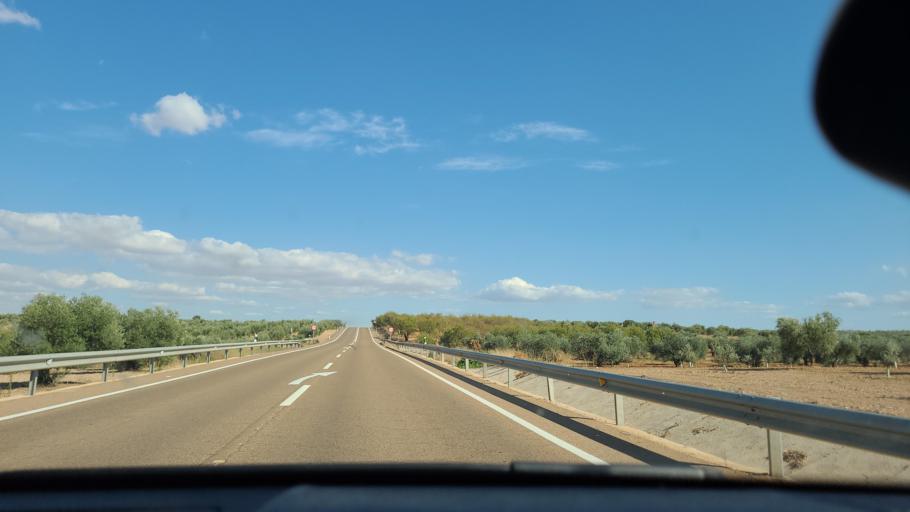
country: ES
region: Extremadura
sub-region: Provincia de Badajoz
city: Usagre
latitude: 38.3474
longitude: -6.1868
